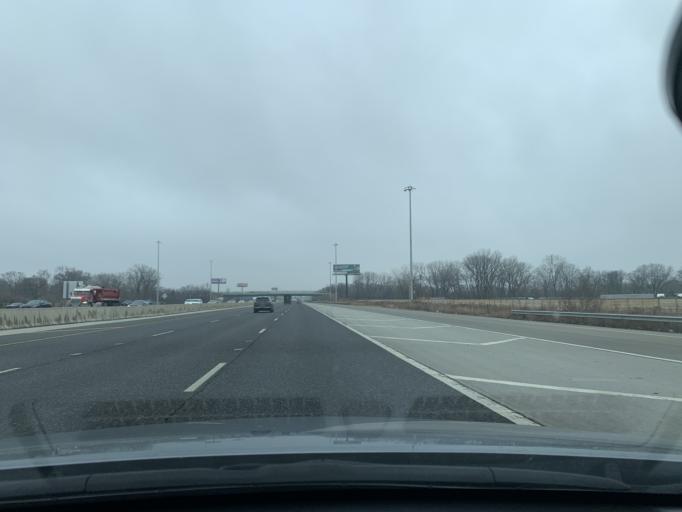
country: US
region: Illinois
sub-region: Cook County
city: Posen
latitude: 41.6146
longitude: -87.6925
